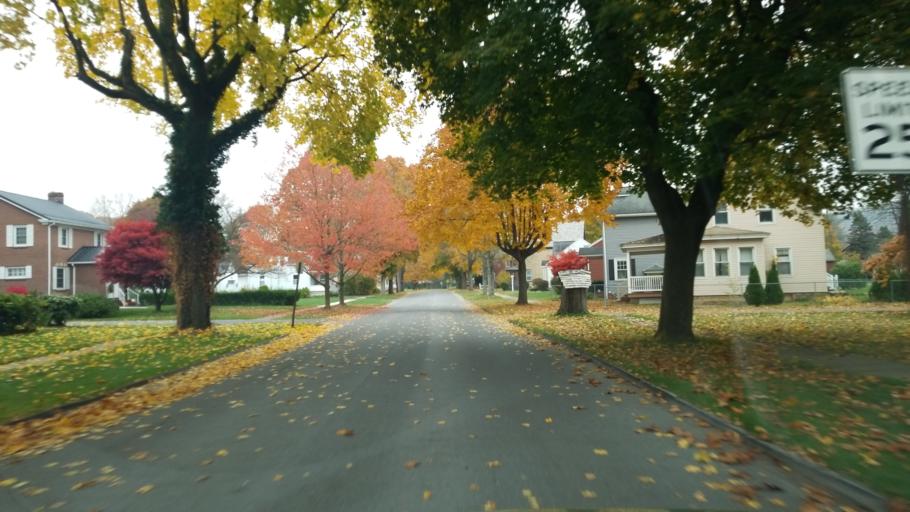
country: US
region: Pennsylvania
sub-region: Clearfield County
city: Hyde
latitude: 41.0103
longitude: -78.4474
